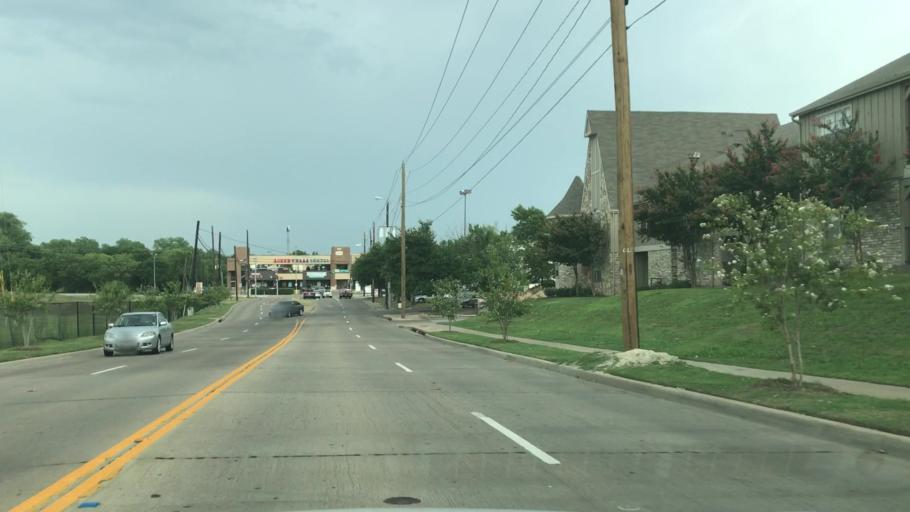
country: US
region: Texas
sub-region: Dallas County
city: University Park
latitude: 32.8684
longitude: -96.7448
